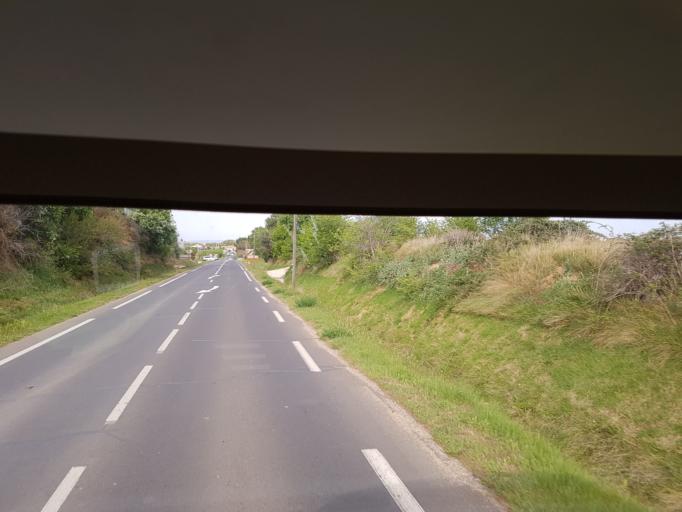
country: FR
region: Languedoc-Roussillon
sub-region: Departement de l'Herault
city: Marseillan
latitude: 43.3517
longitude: 3.5144
